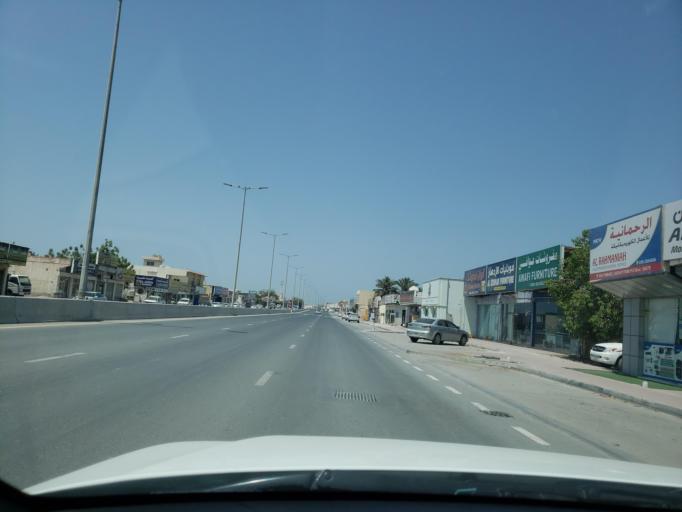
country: AE
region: Ra's al Khaymah
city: Ras al-Khaimah
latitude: 25.8151
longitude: 55.9752
